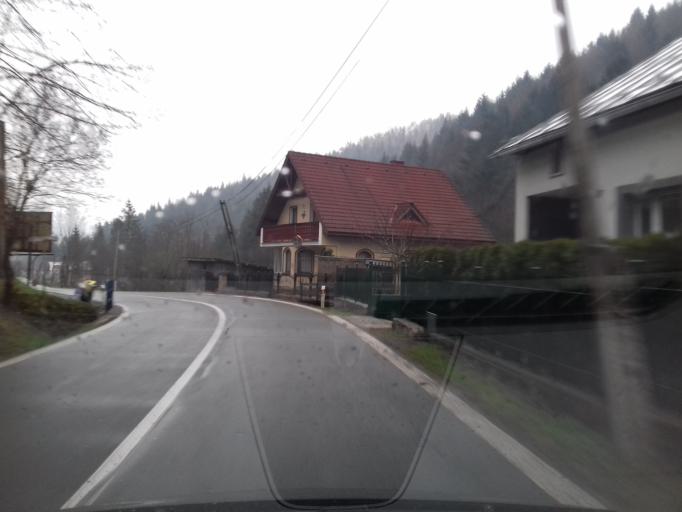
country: PL
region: Lesser Poland Voivodeship
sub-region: Powiat nowosadecki
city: Piwniczna-Zdroj
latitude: 49.4077
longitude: 20.7052
